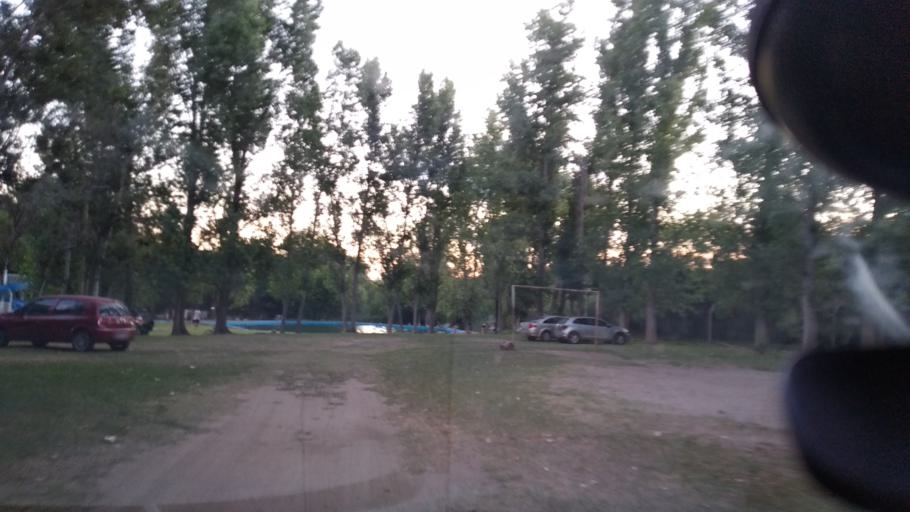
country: AR
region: Cordoba
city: Villa Las Rosas
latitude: -31.9443
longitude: -65.0699
